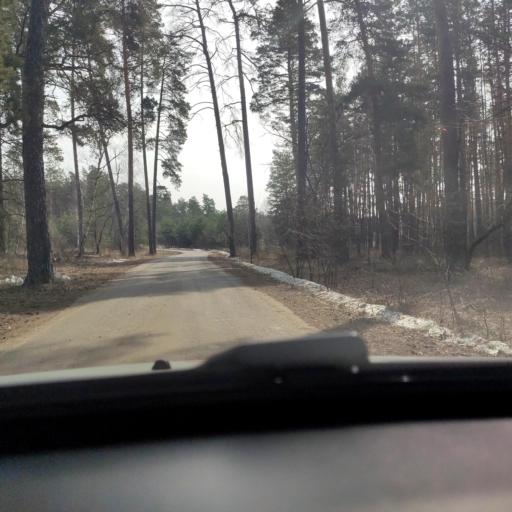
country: RU
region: Voronezj
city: Ramon'
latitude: 51.8912
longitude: 39.3662
